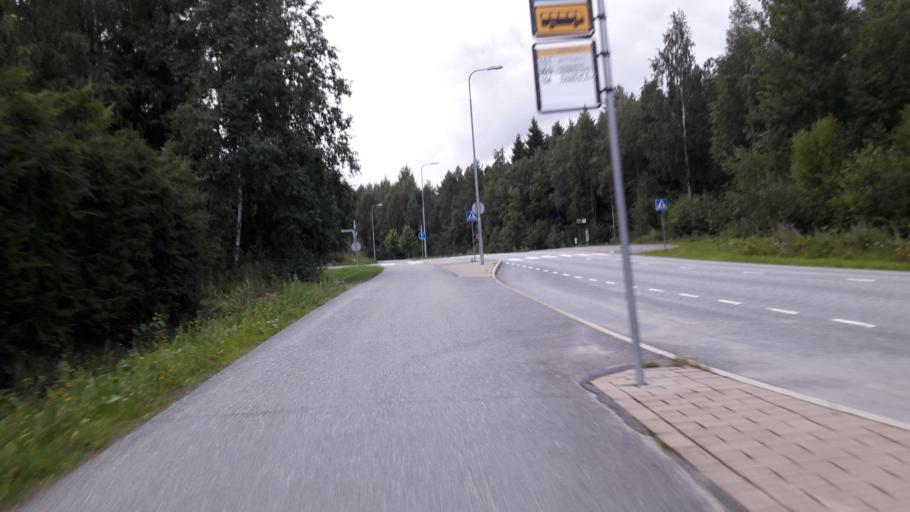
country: FI
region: North Karelia
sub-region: Joensuu
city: Joensuu
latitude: 62.5338
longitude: 29.8410
